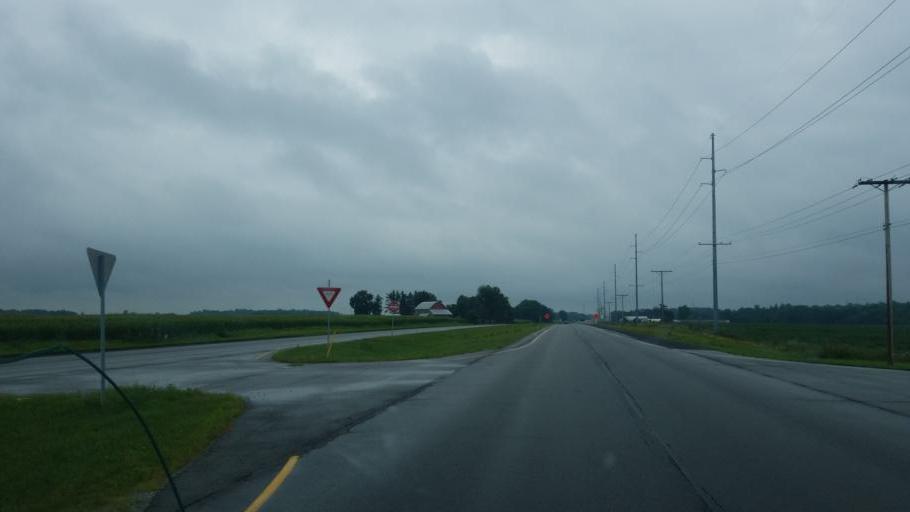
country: US
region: Indiana
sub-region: Allen County
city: New Haven
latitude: 40.9368
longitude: -85.0409
